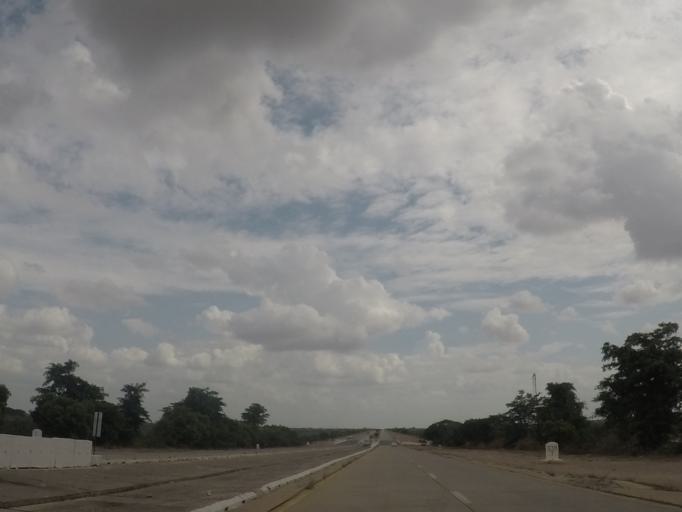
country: MM
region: Mandalay
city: Kyaukse
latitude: 21.5712
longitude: 95.9582
